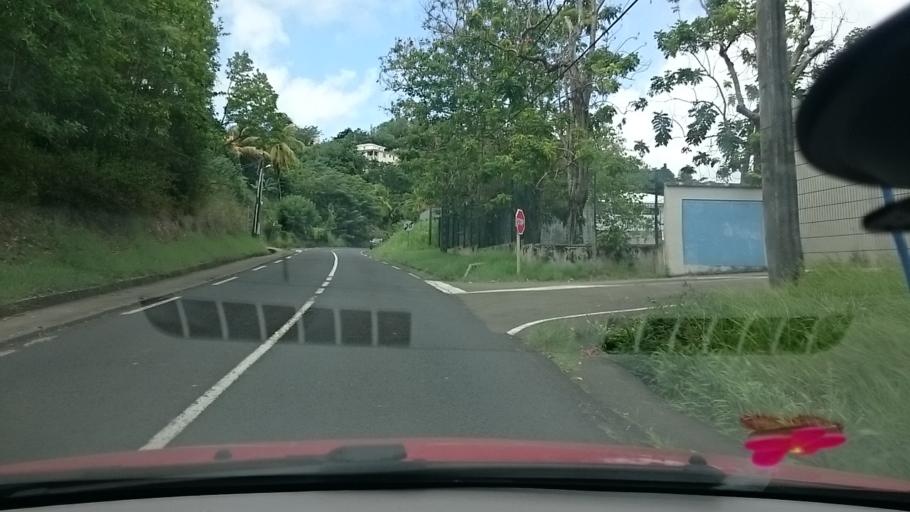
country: MQ
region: Martinique
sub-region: Martinique
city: La Trinite
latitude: 14.7410
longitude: -60.9484
